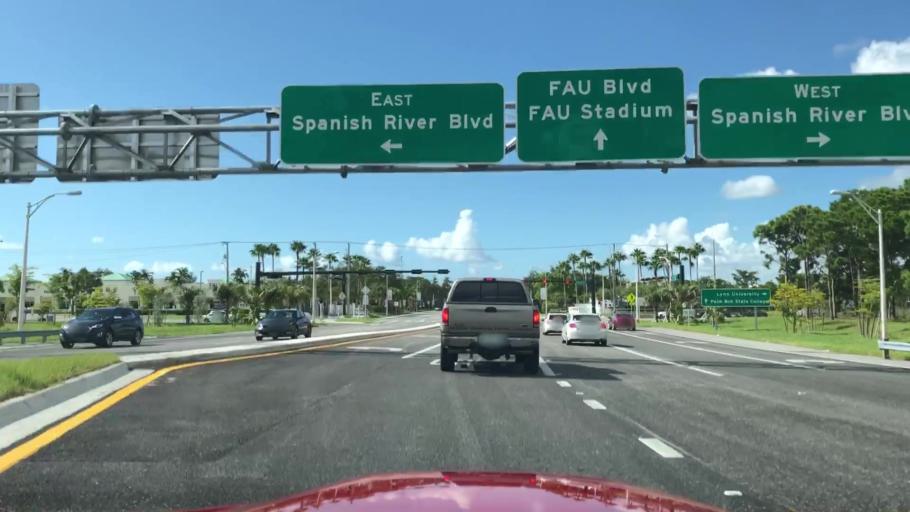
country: US
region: Florida
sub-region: Palm Beach County
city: Boca Raton
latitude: 26.3873
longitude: -80.0980
